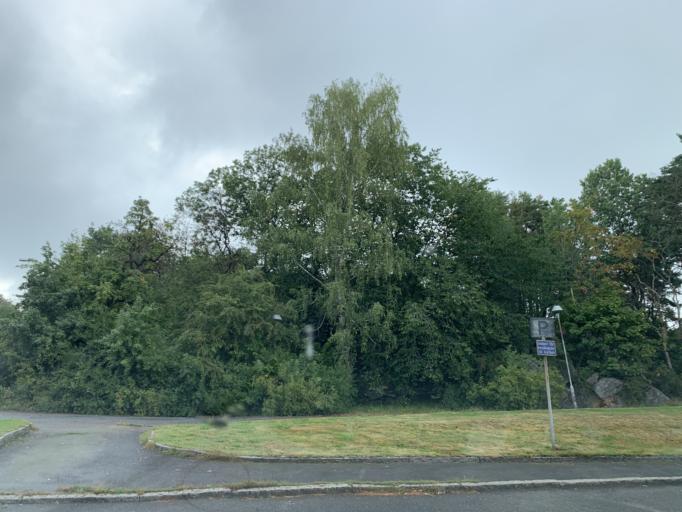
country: SE
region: Vaestra Goetaland
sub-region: Goteborg
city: Eriksbo
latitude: 57.7484
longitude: 12.0275
